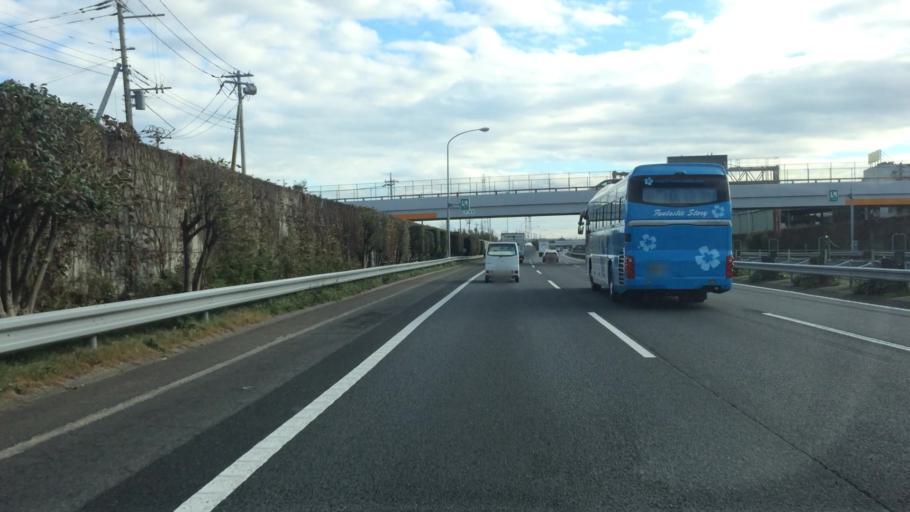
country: JP
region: Chiba
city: Yotsukaido
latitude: 35.6820
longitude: 140.1496
